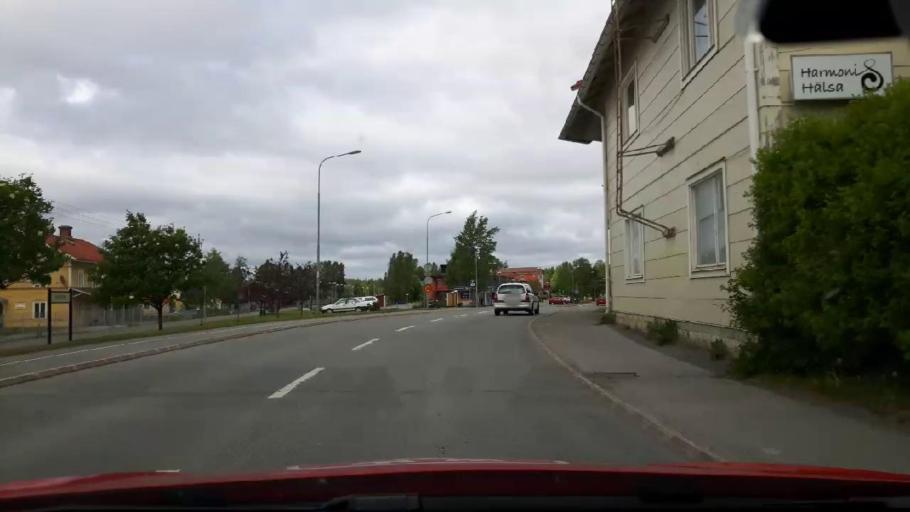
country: SE
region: Jaemtland
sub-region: Krokoms Kommun
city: Krokom
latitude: 63.3255
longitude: 14.4491
